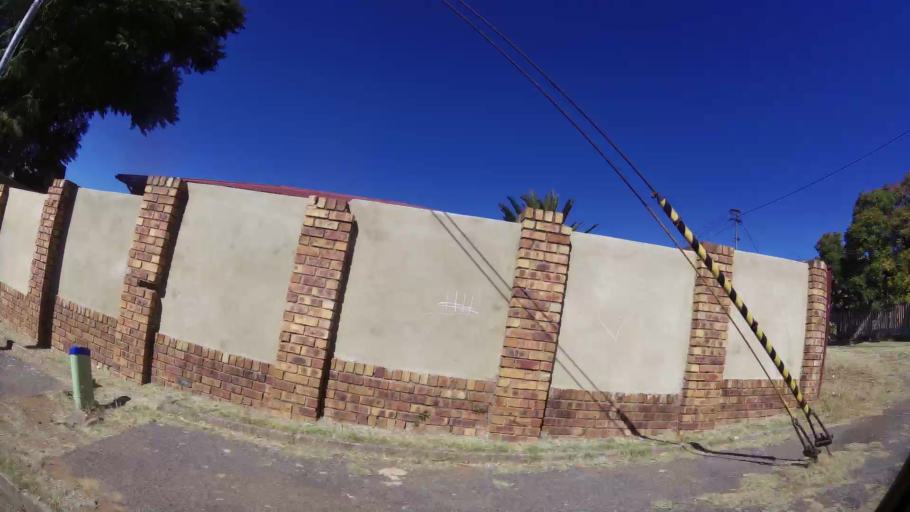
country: ZA
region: Gauteng
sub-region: City of Johannesburg Metropolitan Municipality
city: Johannesburg
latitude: -26.2549
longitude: 28.0875
